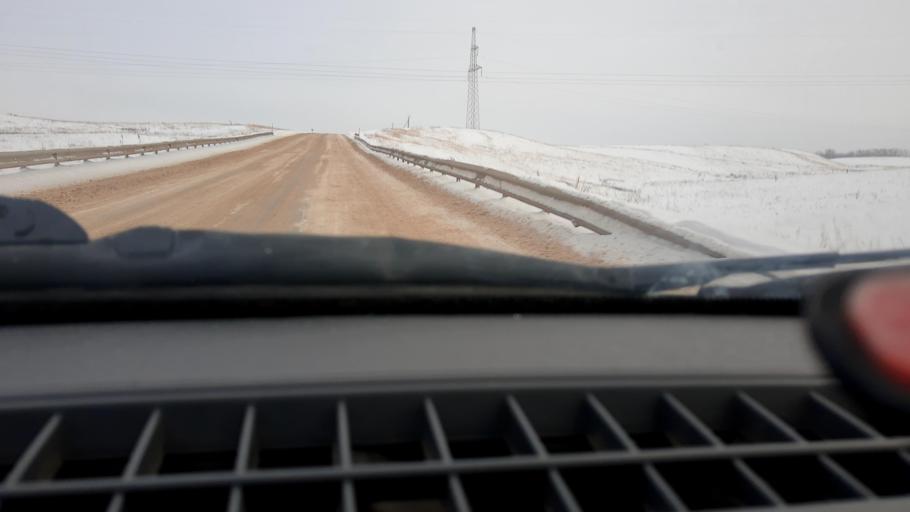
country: RU
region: Bashkortostan
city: Alekseyevka
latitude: 54.6785
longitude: 55.0119
